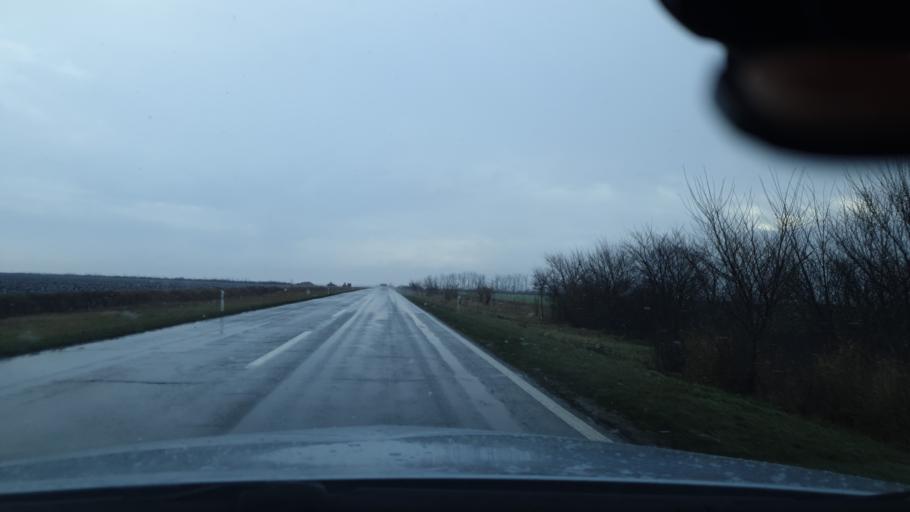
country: RS
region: Autonomna Pokrajina Vojvodina
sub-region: Juznobanatski Okrug
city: Pancevo
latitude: 44.8468
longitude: 20.7820
